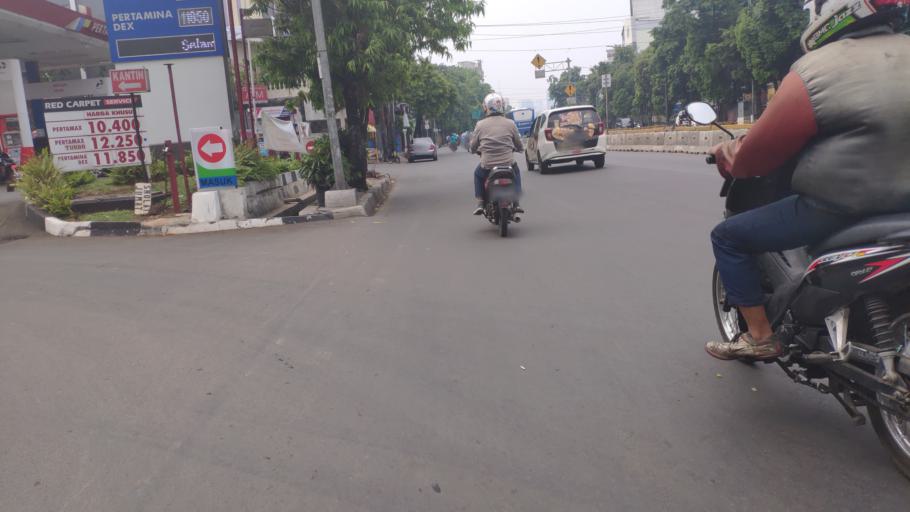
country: ID
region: Jakarta Raya
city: Jakarta
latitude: -6.2617
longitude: 106.8292
